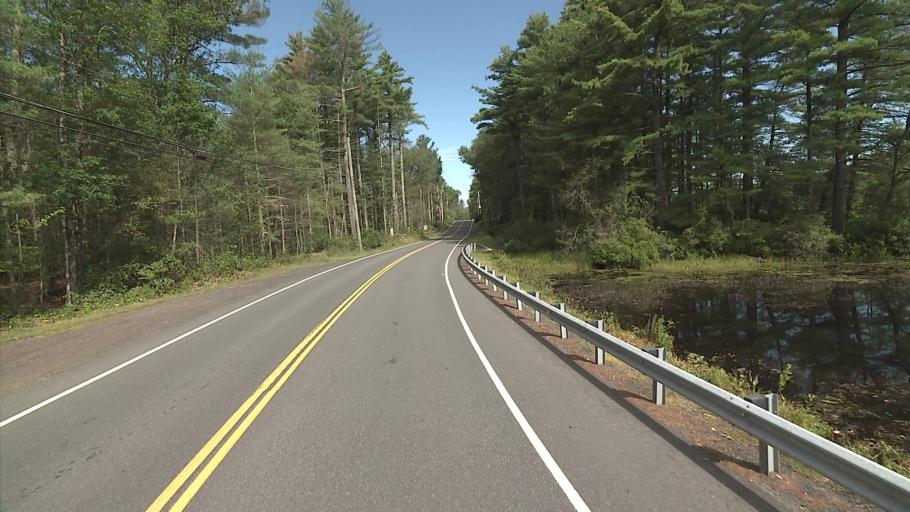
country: US
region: Connecticut
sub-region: Tolland County
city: Stafford
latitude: 42.0159
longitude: -72.3173
